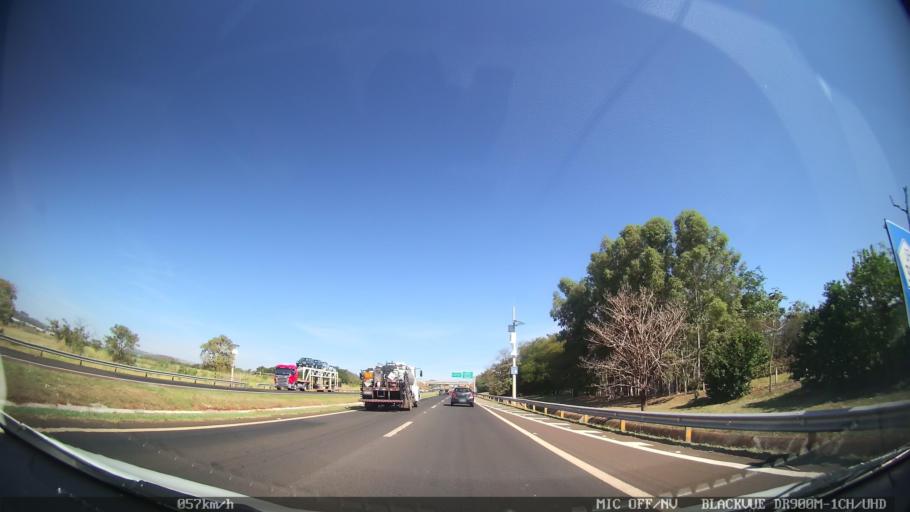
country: BR
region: Sao Paulo
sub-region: Ribeirao Preto
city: Ribeirao Preto
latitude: -21.2184
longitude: -47.7746
